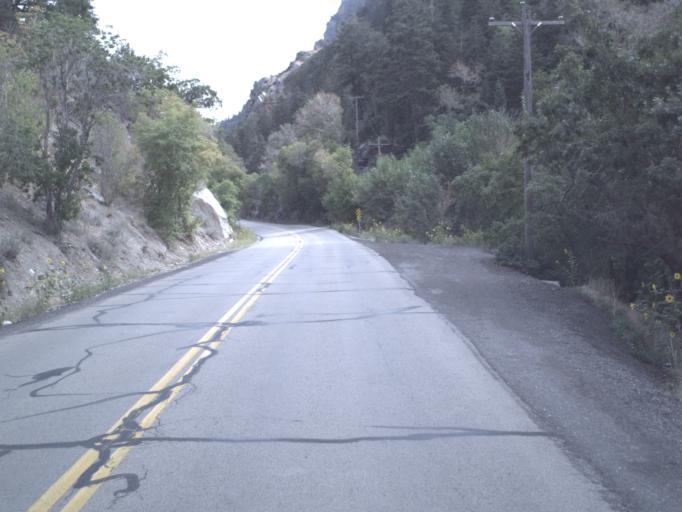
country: US
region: Utah
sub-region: Utah County
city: Cedar Hills
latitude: 40.4360
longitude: -111.7289
